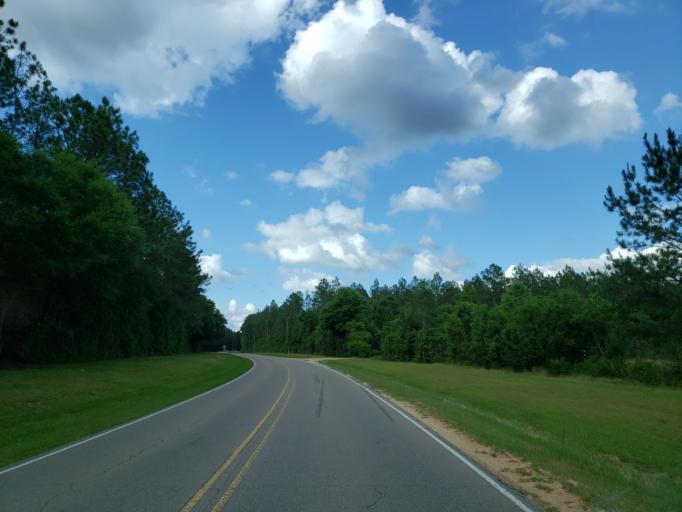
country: US
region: Mississippi
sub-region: Forrest County
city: Petal
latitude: 31.2654
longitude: -89.2140
